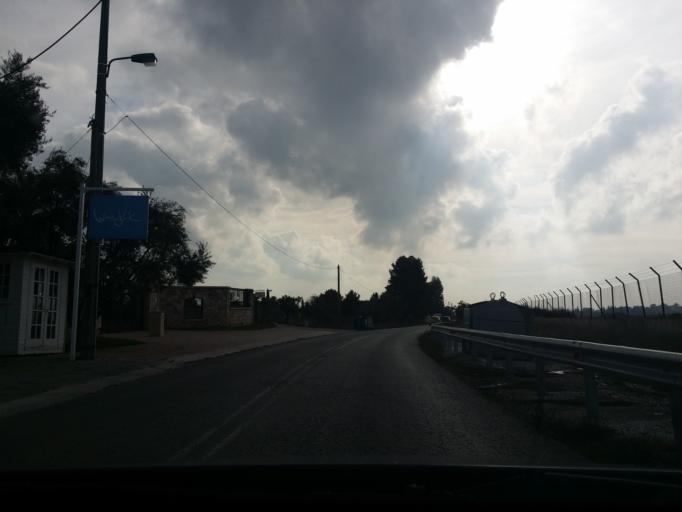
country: GR
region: Attica
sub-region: Nomarchia Anatolikis Attikis
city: Varybobi
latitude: 38.1096
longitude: 23.7907
